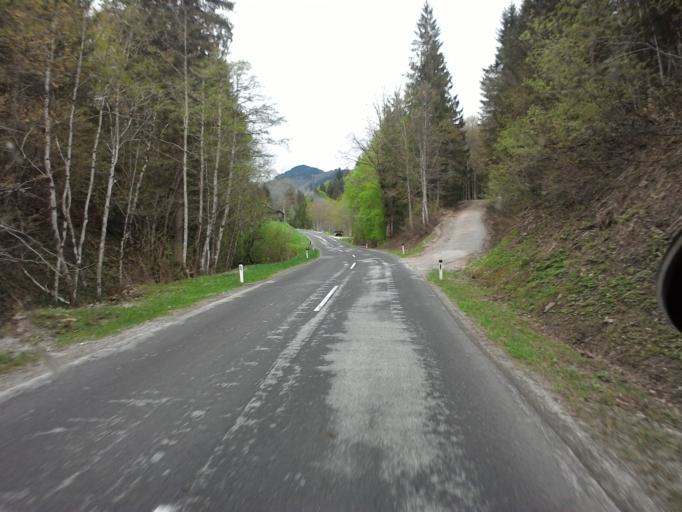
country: AT
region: Styria
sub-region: Politischer Bezirk Liezen
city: Hall
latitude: 47.7081
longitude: 14.4375
